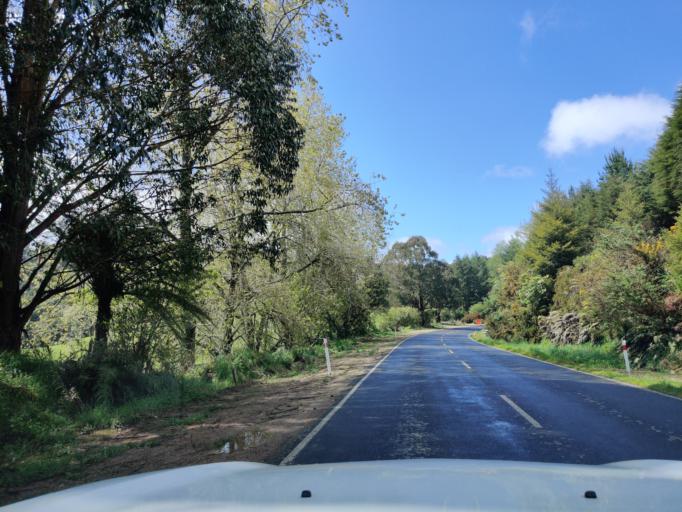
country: NZ
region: Bay of Plenty
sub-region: Rotorua District
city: Rotorua
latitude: -38.1747
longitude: 176.3244
